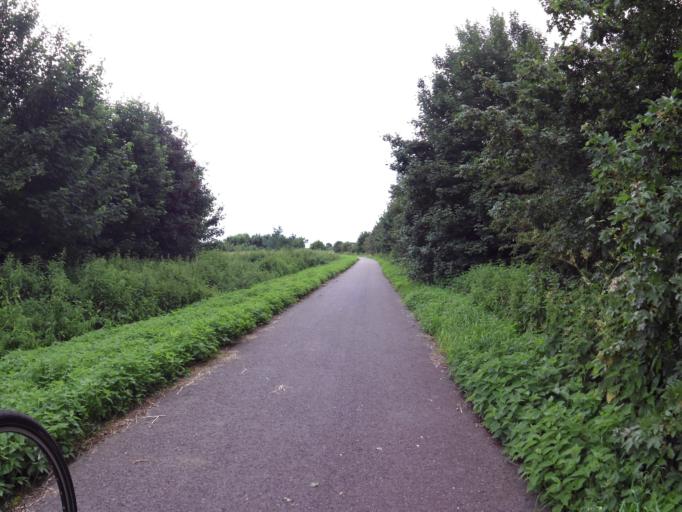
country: NL
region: North Brabant
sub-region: Gemeente Landerd
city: Reek
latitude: 51.7696
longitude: 5.6773
